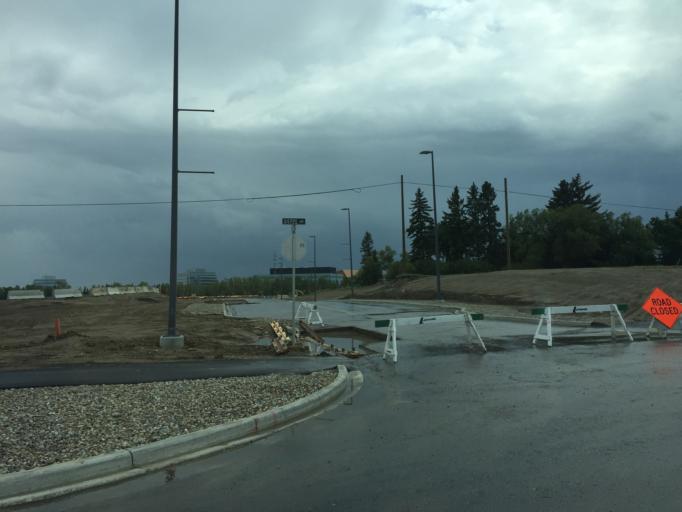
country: CA
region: Alberta
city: Calgary
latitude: 51.0178
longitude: -114.1264
